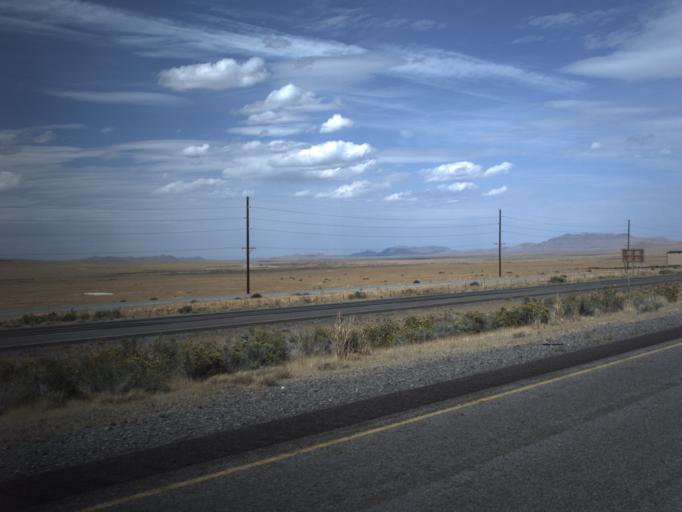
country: US
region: Utah
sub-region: Tooele County
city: Grantsville
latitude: 40.7807
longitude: -112.9676
